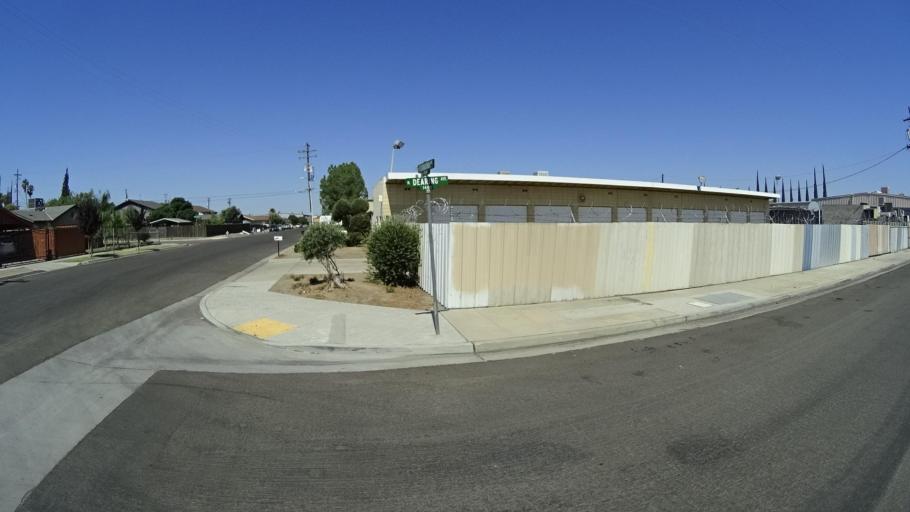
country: US
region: California
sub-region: Fresno County
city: Fresno
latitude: 36.7615
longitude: -119.7380
